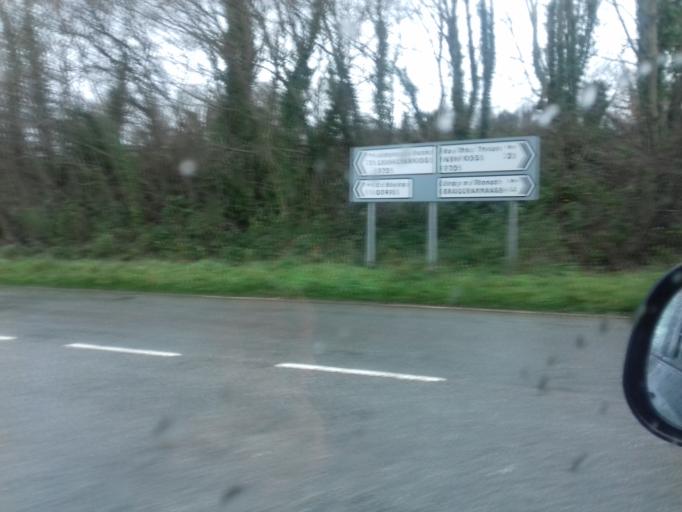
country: IE
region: Leinster
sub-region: Kilkenny
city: Graiguenamanagh
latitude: 52.5789
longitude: -6.9518
